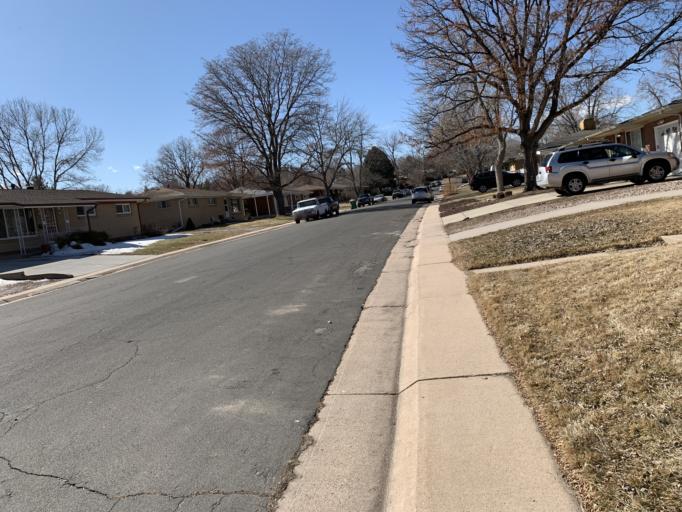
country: US
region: Colorado
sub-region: Arapahoe County
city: Littleton
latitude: 39.6194
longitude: -105.0323
